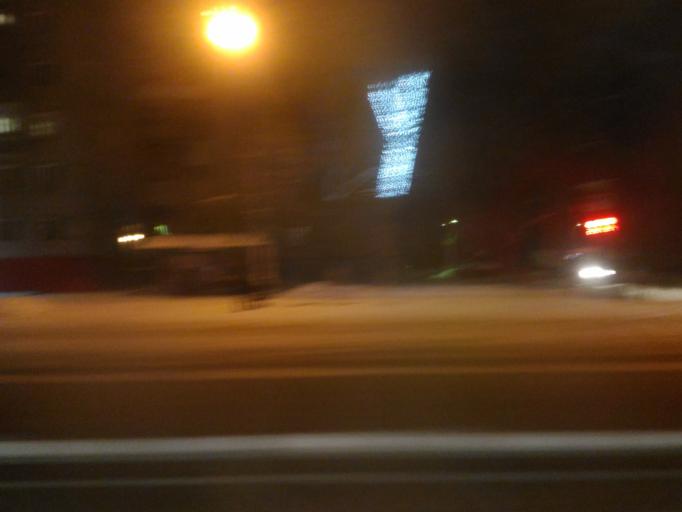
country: RU
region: Ulyanovsk
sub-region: Ulyanovskiy Rayon
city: Ulyanovsk
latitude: 54.3481
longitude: 48.3690
